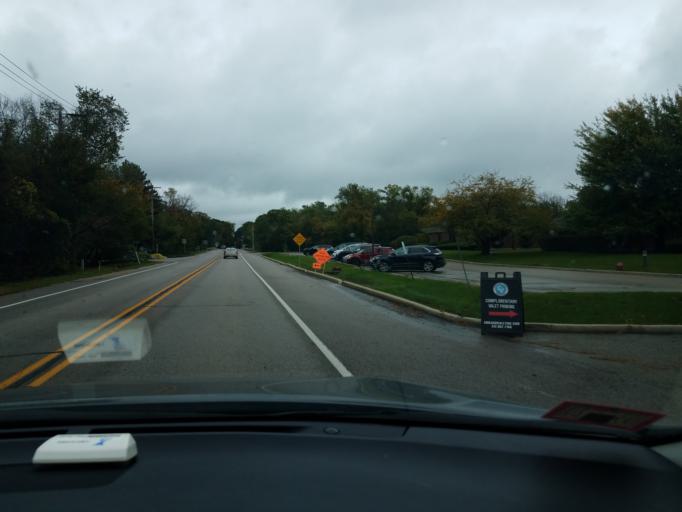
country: US
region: Illinois
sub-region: Lake County
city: Riverwoods
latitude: 42.1677
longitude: -87.9165
